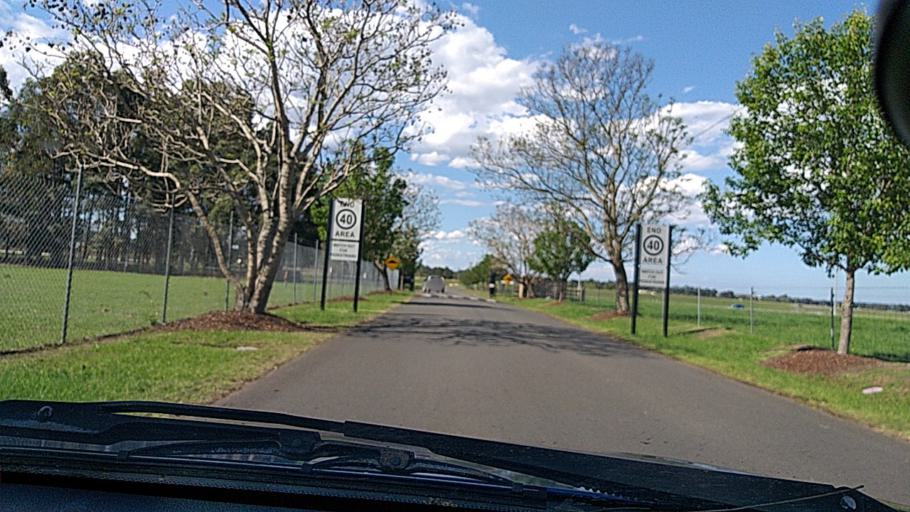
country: AU
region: New South Wales
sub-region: Hawkesbury
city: Richmond
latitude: -33.6126
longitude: 150.7595
